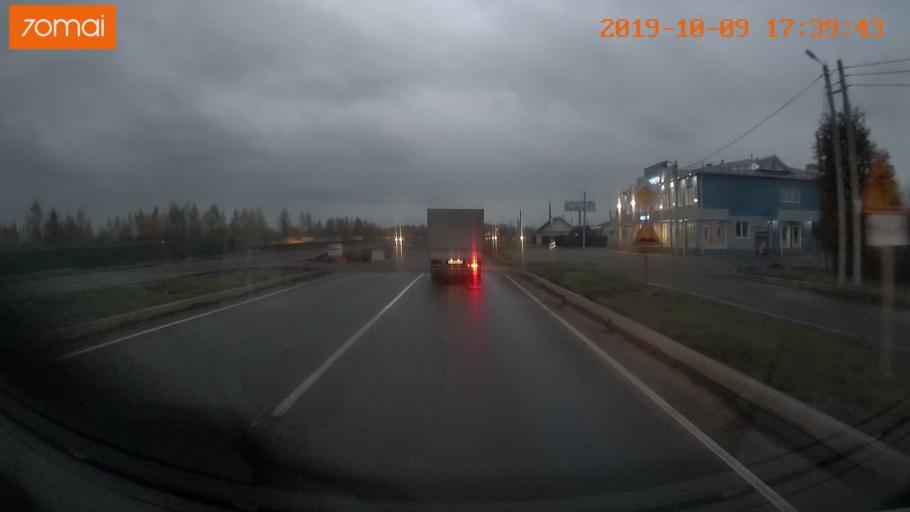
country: RU
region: Ivanovo
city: Bogorodskoye
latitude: 57.0584
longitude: 40.9610
